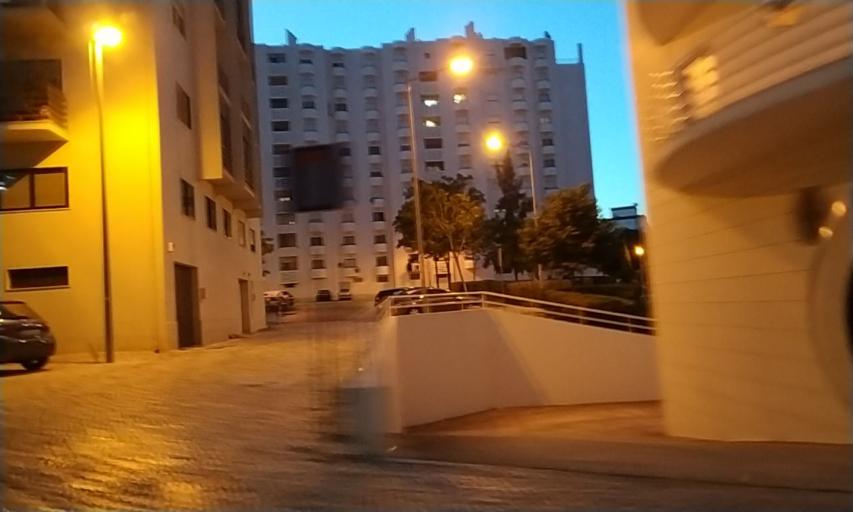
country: PT
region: Setubal
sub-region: Setubal
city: Setubal
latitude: 38.5395
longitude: -8.8928
